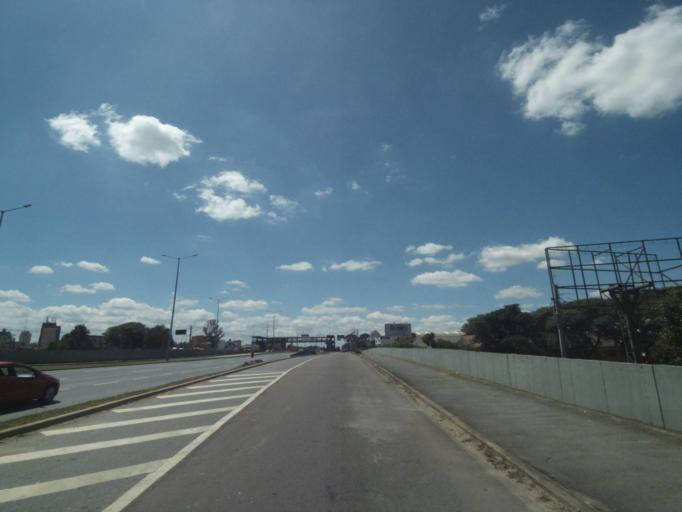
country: BR
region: Parana
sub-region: Sao Jose Dos Pinhais
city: Sao Jose dos Pinhais
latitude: -25.5231
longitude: -49.2952
